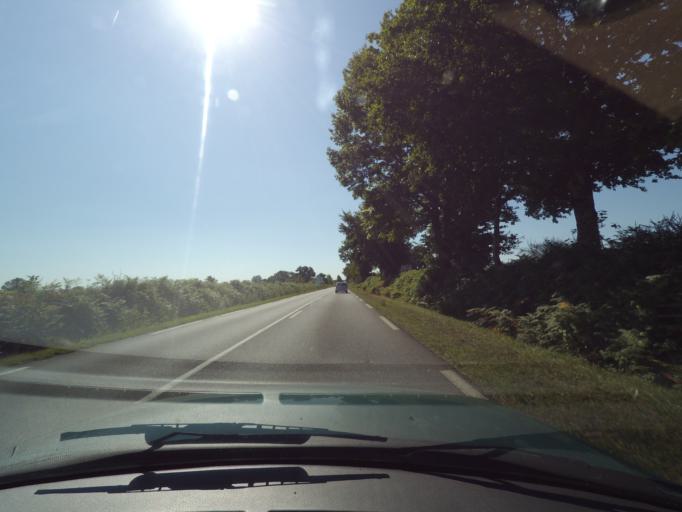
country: FR
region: Limousin
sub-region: Departement de la Haute-Vienne
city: Peyrat-de-Bellac
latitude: 46.1339
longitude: 0.9864
